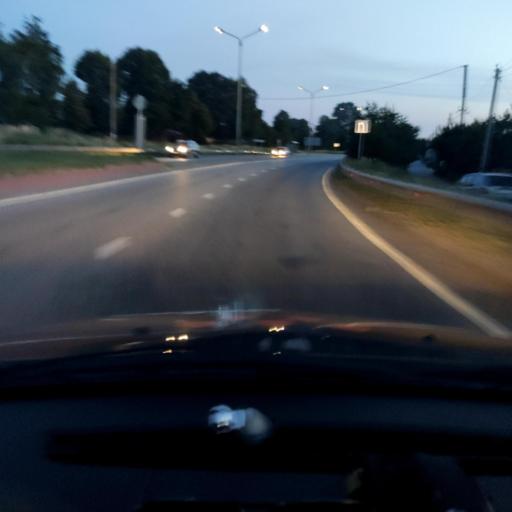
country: RU
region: Belgorod
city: Gubkin
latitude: 51.2776
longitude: 37.5932
